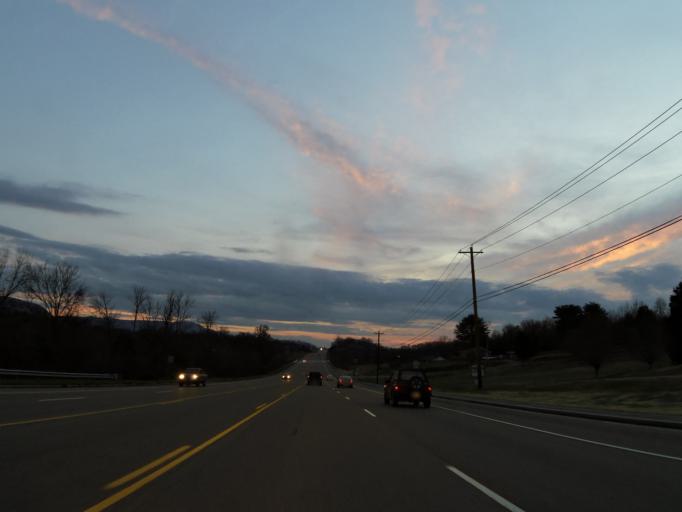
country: US
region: Tennessee
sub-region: McMinn County
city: Etowah
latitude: 35.3049
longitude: -84.5355
